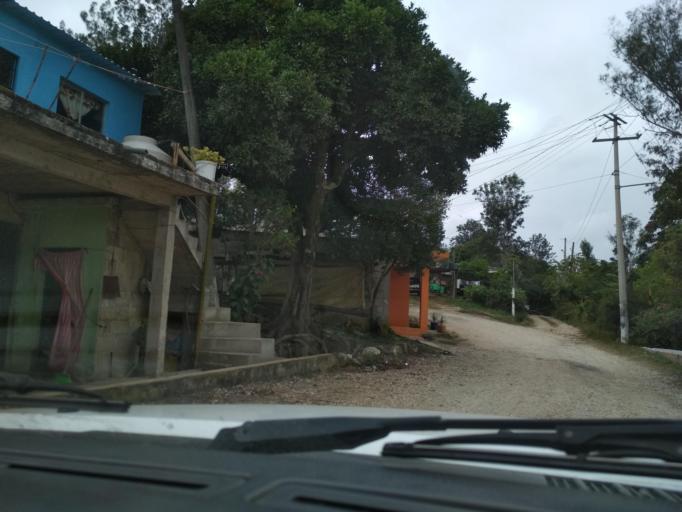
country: MX
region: Veracruz
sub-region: Emiliano Zapata
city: Dos Rios
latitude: 19.5382
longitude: -96.7981
